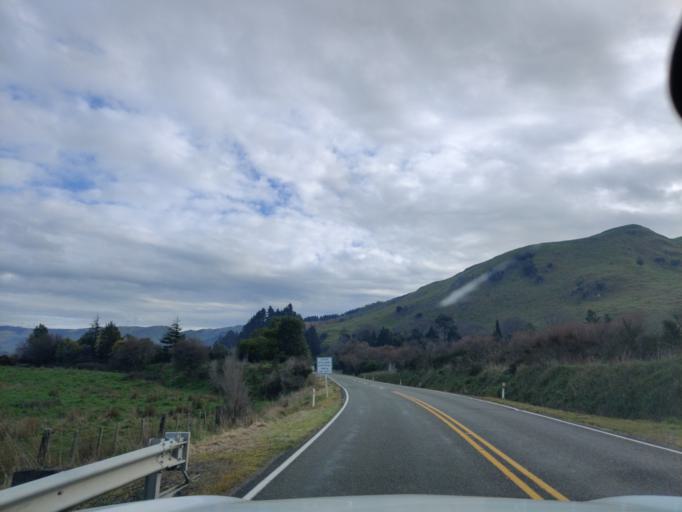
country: NZ
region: Manawatu-Wanganui
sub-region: Palmerston North City
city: Palmerston North
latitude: -40.3361
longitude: 175.8366
